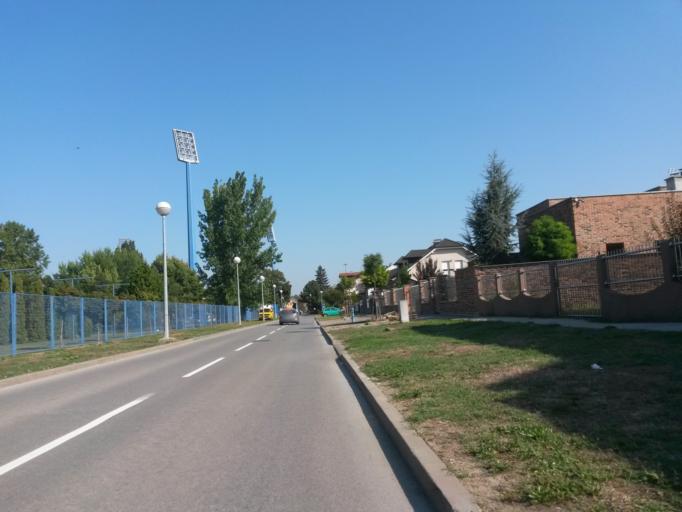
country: HR
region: Osjecko-Baranjska
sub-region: Grad Osijek
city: Osijek
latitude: 45.5428
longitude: 18.6970
